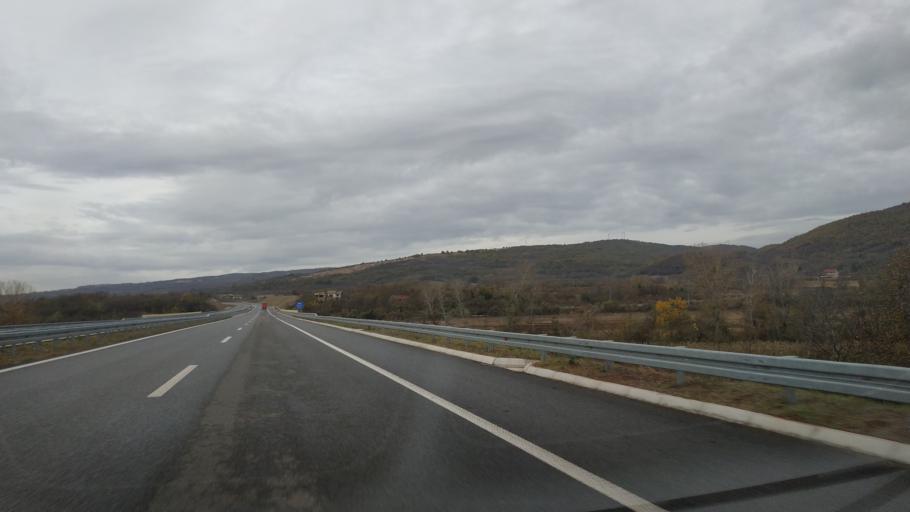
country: RS
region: Central Serbia
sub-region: Nisavski Okrug
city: Niska Banja
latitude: 43.3061
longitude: 22.0397
